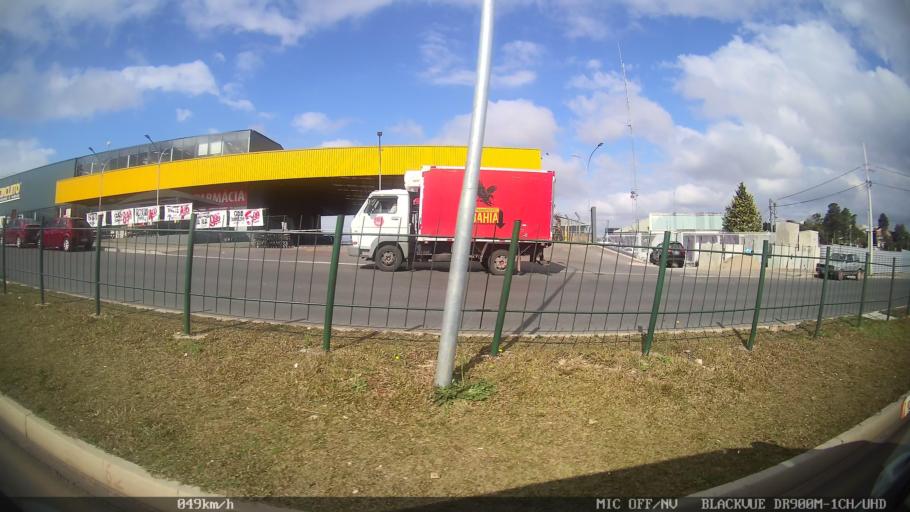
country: BR
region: Parana
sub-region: Pinhais
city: Pinhais
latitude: -25.3805
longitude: -49.1839
